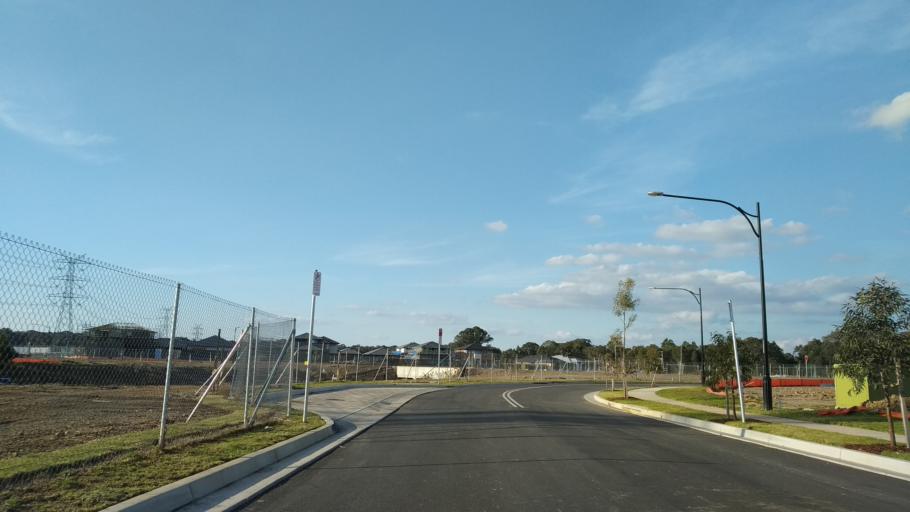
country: AU
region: New South Wales
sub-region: Penrith Municipality
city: Werrington County
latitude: -33.7309
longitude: 150.7545
